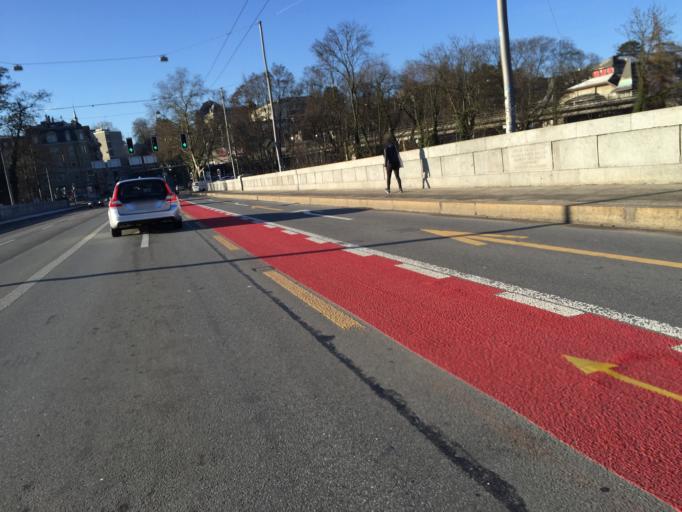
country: CH
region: Bern
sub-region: Bern-Mittelland District
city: Bern
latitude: 46.9529
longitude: 7.4433
